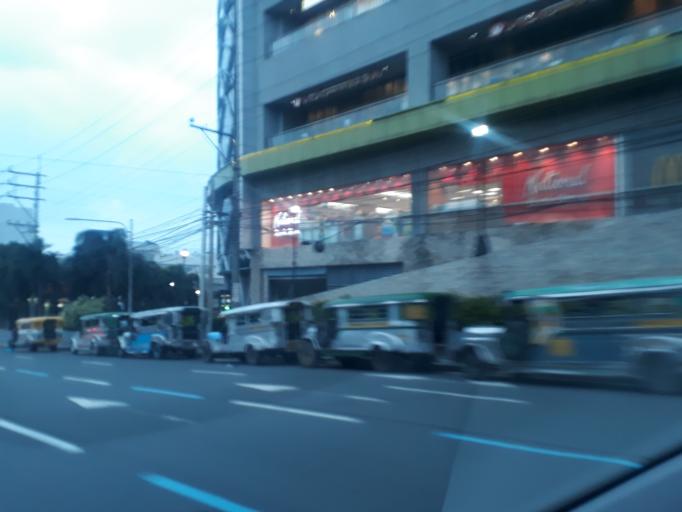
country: PH
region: Calabarzon
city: Del Monte
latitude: 14.6332
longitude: 121.0194
